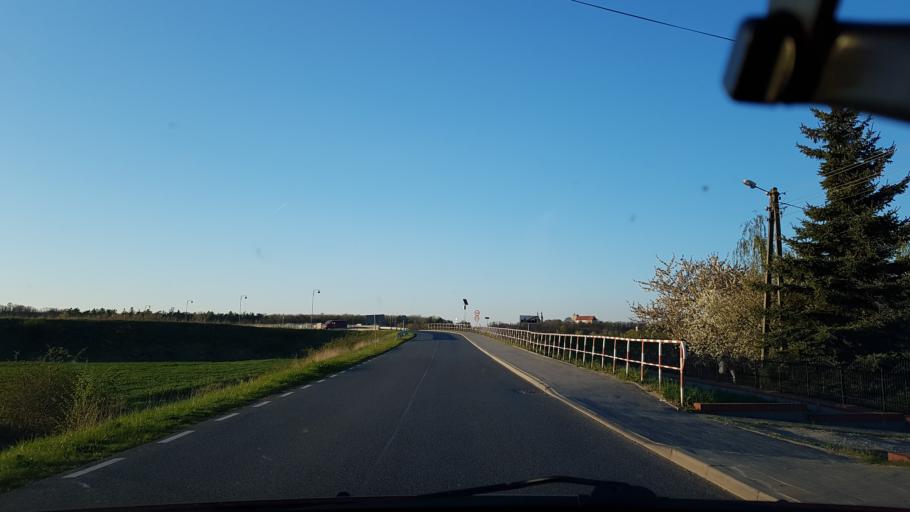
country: PL
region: Opole Voivodeship
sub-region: Powiat nyski
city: Otmuchow
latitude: 50.4512
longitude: 17.1659
